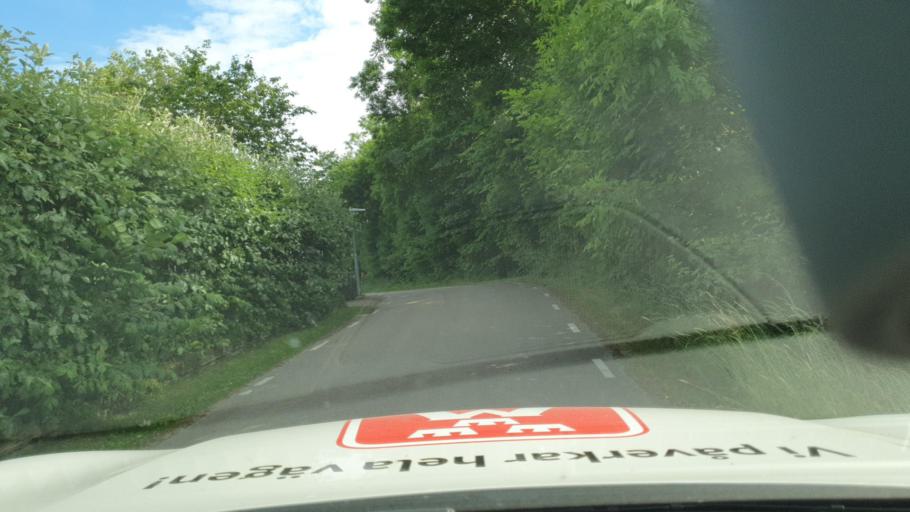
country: SE
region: Skane
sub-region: Skurups Kommun
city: Rydsgard
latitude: 55.4490
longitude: 13.5939
